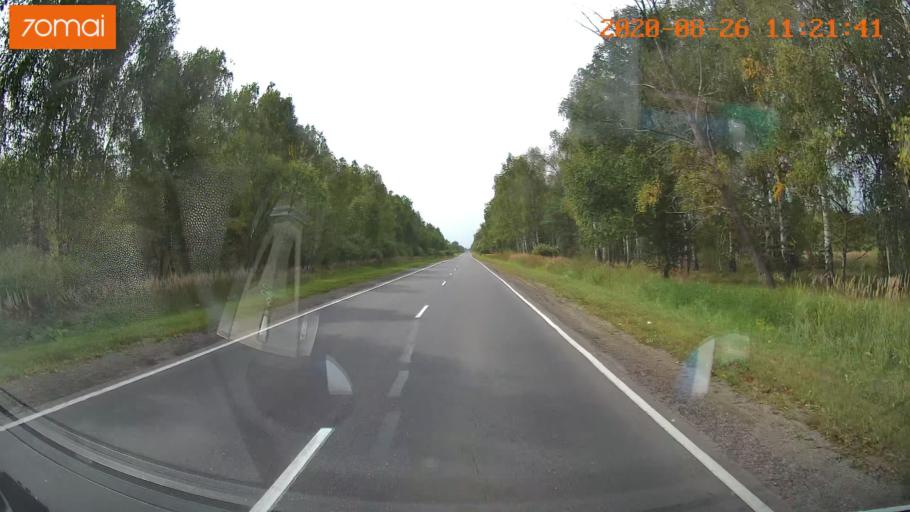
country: RU
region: Rjazan
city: Shilovo
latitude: 54.3733
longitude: 41.0406
